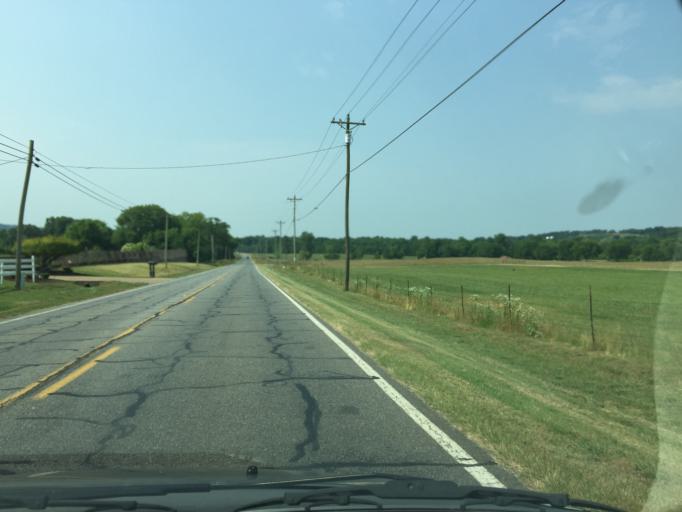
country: US
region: Georgia
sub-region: Catoosa County
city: Ringgold
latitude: 34.9682
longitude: -85.1015
